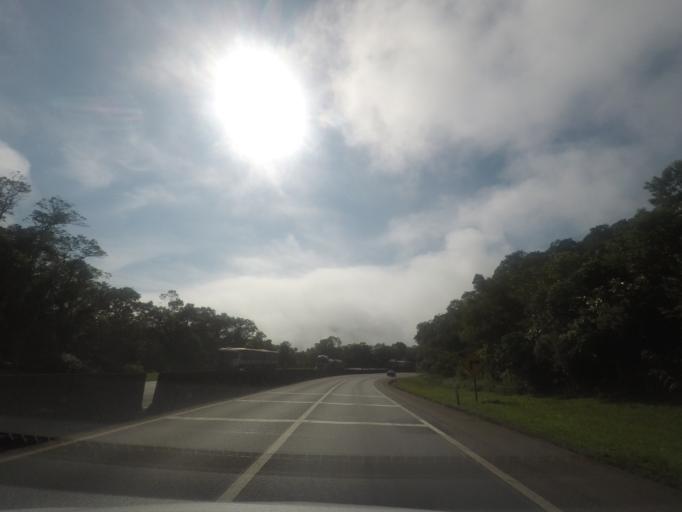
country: BR
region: Parana
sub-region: Piraquara
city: Piraquara
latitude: -25.5925
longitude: -48.8887
